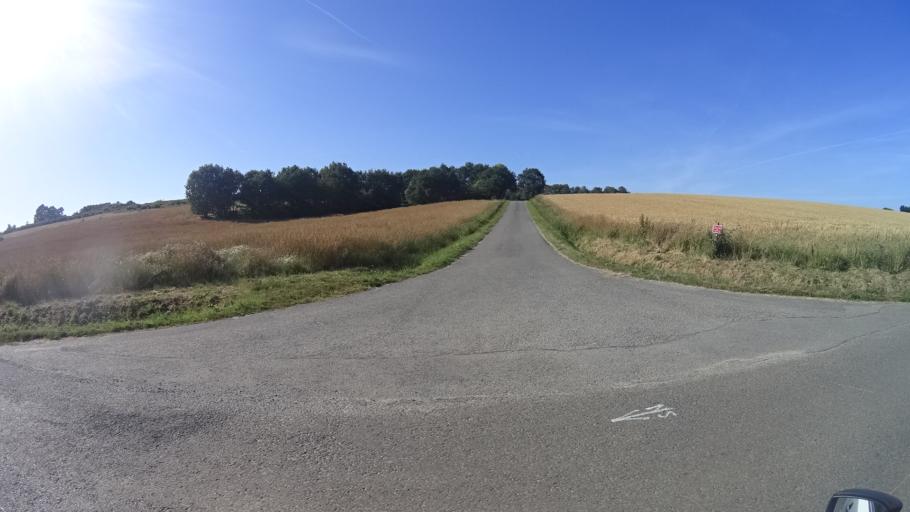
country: FR
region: Brittany
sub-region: Departement d'Ille-et-Vilaine
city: Langon
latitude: 47.7122
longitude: -1.8636
